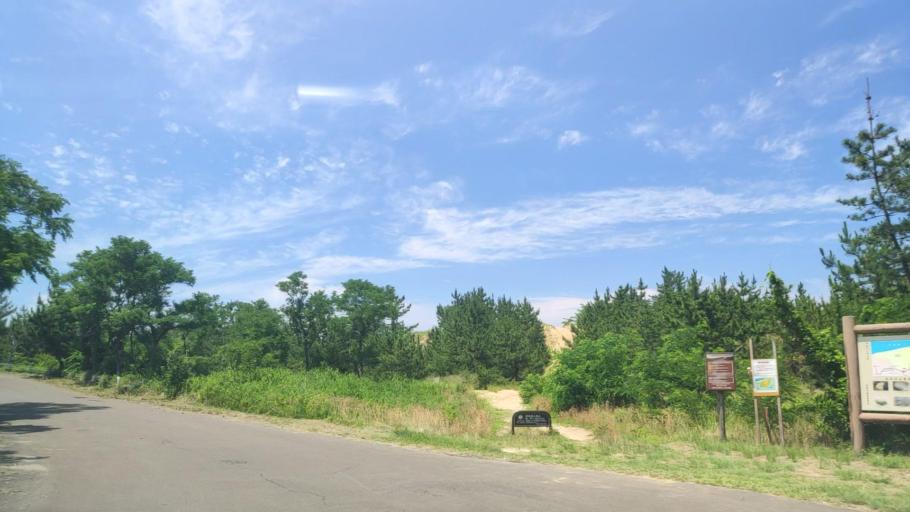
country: JP
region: Tottori
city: Tottori
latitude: 35.5346
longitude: 134.2304
